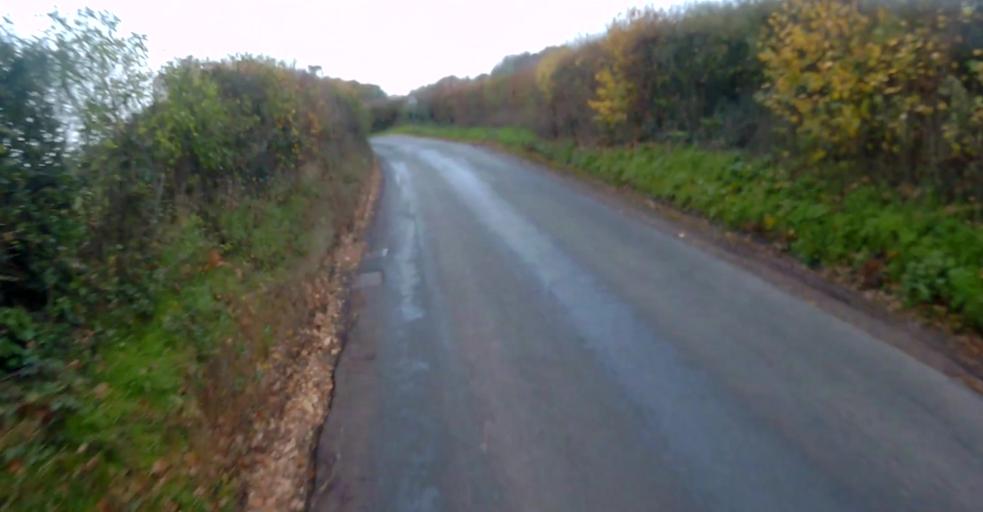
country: GB
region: England
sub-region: Wokingham
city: Swallowfield
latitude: 51.3805
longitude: -0.9346
